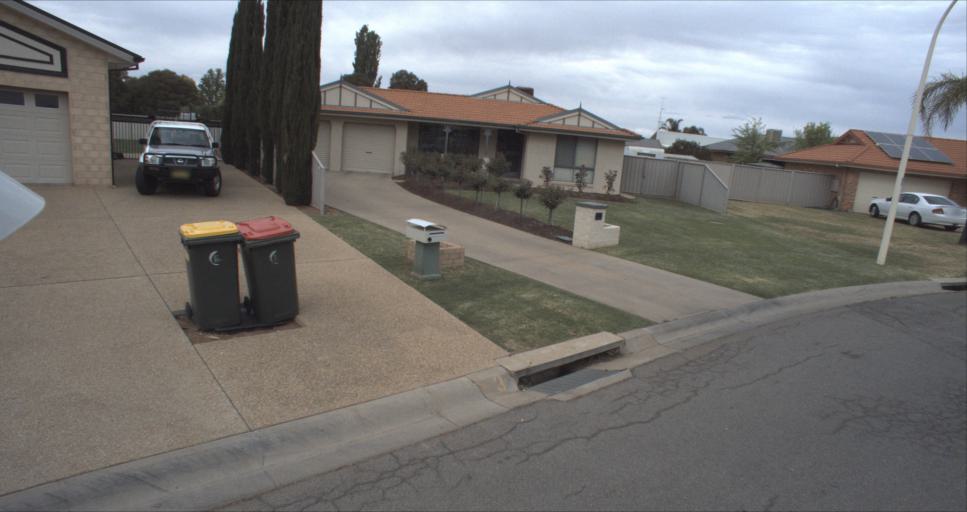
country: AU
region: New South Wales
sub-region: Leeton
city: Leeton
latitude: -34.5411
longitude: 146.4016
